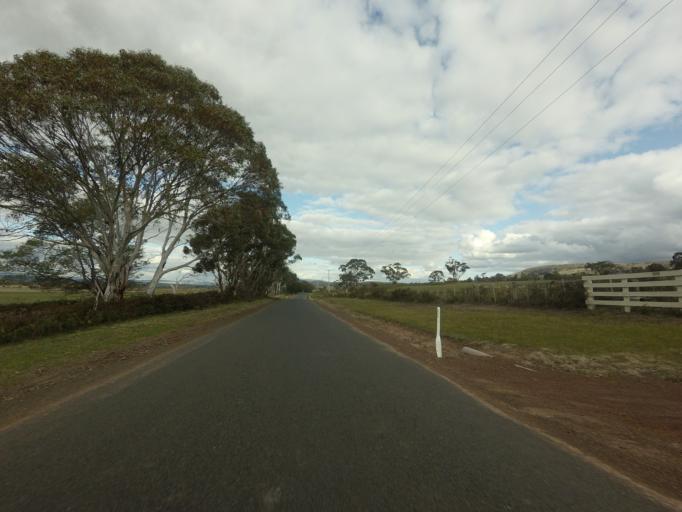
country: AU
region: Tasmania
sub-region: Northern Midlands
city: Evandale
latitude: -41.8740
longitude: 147.3013
